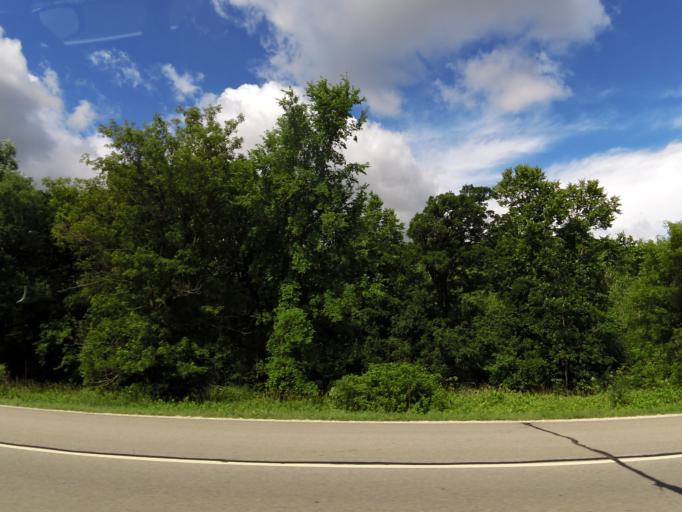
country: US
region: Minnesota
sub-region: Olmsted County
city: Rochester
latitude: 43.9452
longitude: -92.4682
